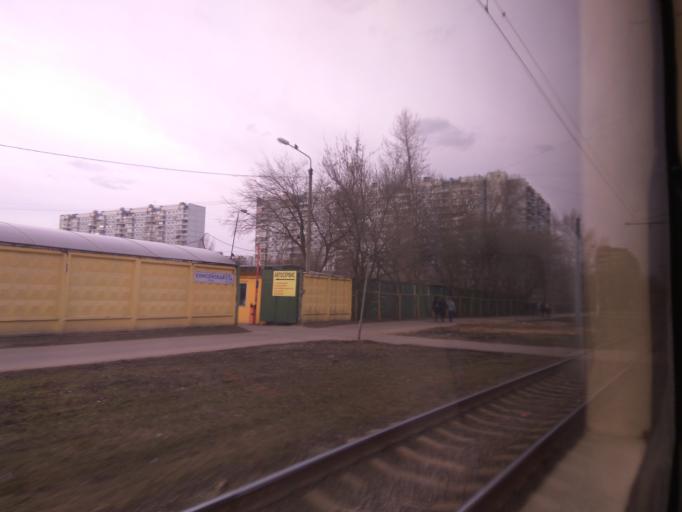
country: RU
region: Moscow
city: Leonovo
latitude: 55.8624
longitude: 37.6605
